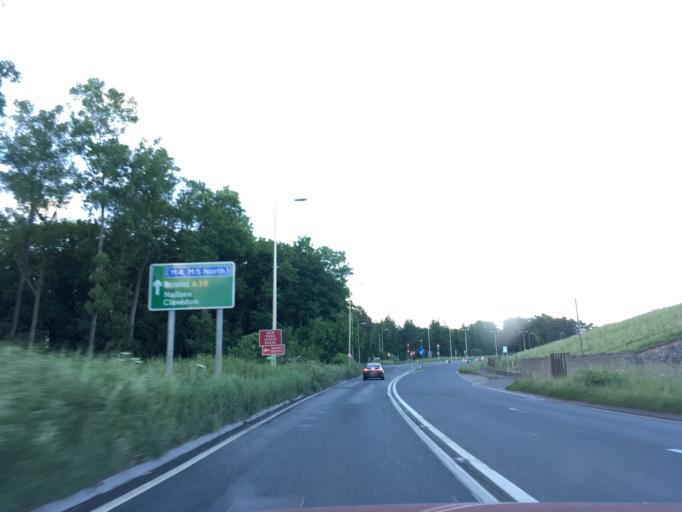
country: GB
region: England
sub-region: North Somerset
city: Winford
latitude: 51.4047
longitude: -2.6692
